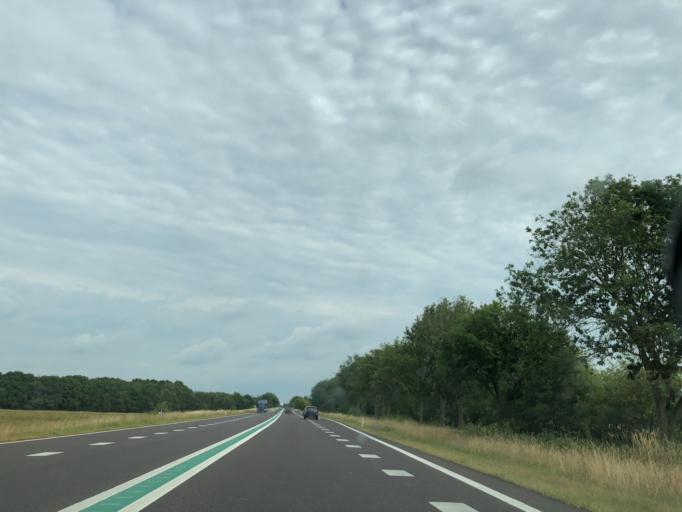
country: NL
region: Drenthe
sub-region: Gemeente Tynaarlo
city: Tynaarlo
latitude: 53.0892
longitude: 6.6467
